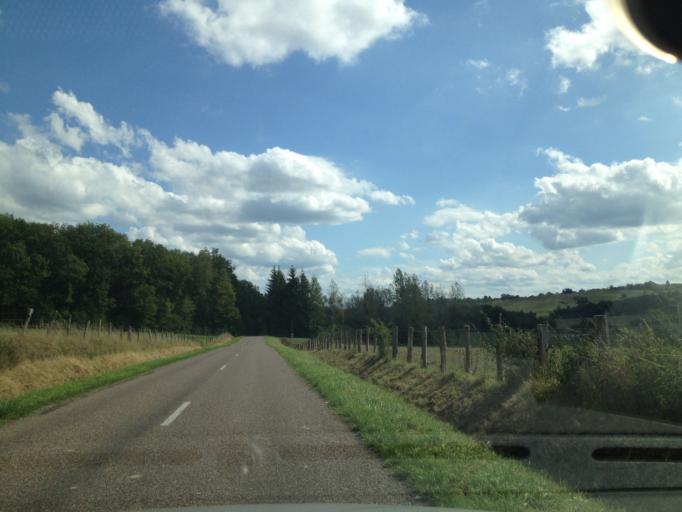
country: FR
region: Franche-Comte
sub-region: Departement de la Haute-Saone
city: Saint-Loup-sur-Semouse
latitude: 47.8666
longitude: 6.1861
